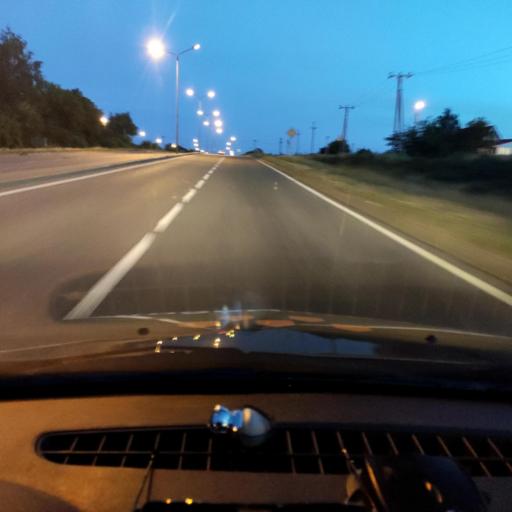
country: RU
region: Belgorod
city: Gubkin
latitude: 51.2563
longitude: 37.5280
